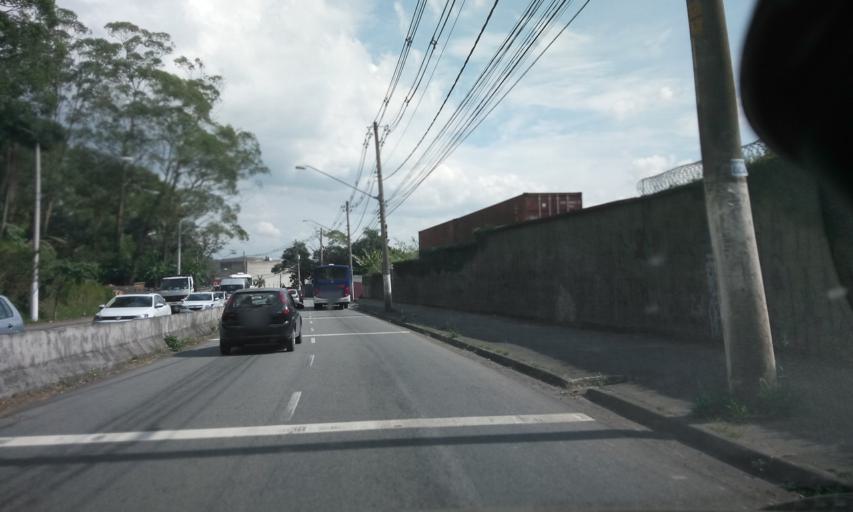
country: BR
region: Sao Paulo
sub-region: Sao Bernardo Do Campo
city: Sao Bernardo do Campo
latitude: -23.7507
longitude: -46.5714
